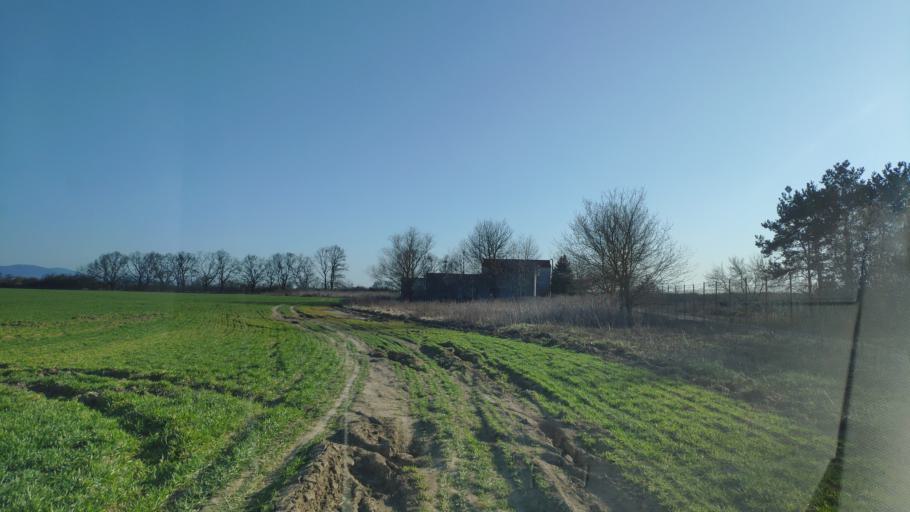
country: SK
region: Kosicky
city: Kosice
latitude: 48.6493
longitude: 21.2415
